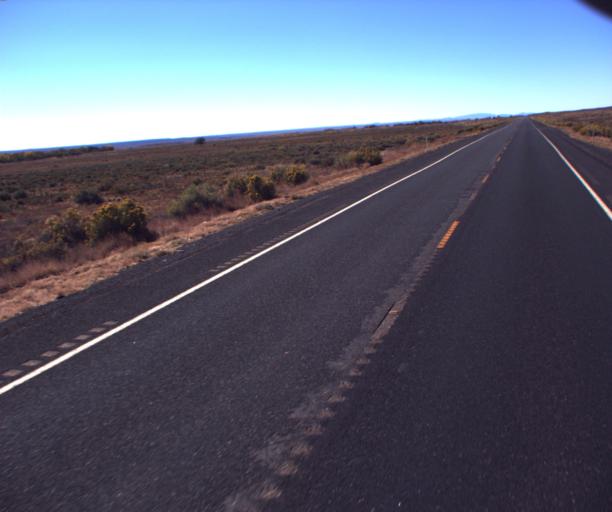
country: US
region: Arizona
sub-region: Coconino County
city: Fredonia
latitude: 36.9410
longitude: -112.5473
